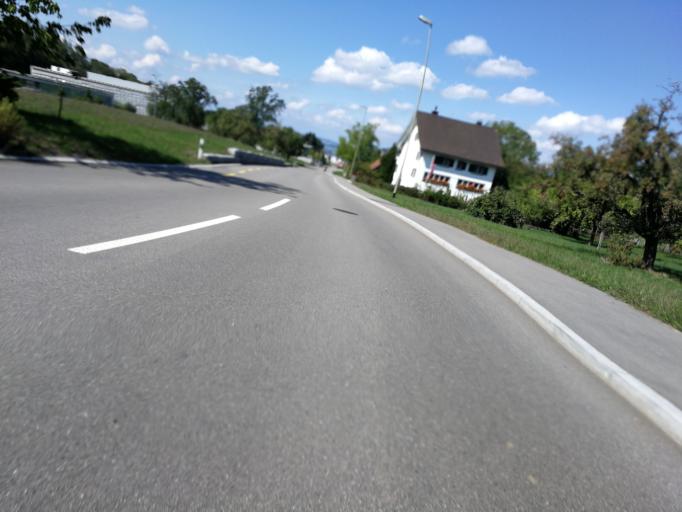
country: CH
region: Zurich
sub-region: Bezirk Horgen
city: Au / Unter-Dorf
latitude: 47.2484
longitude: 8.6197
